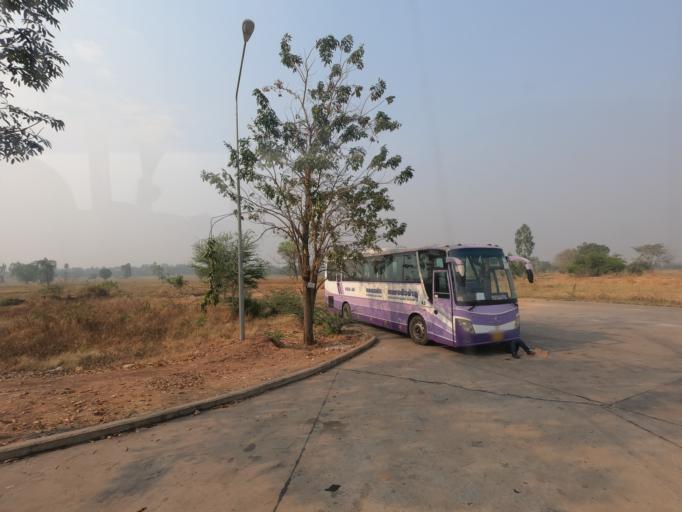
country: TH
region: Khon Kaen
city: Khon Kaen
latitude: 16.3889
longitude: 102.8028
